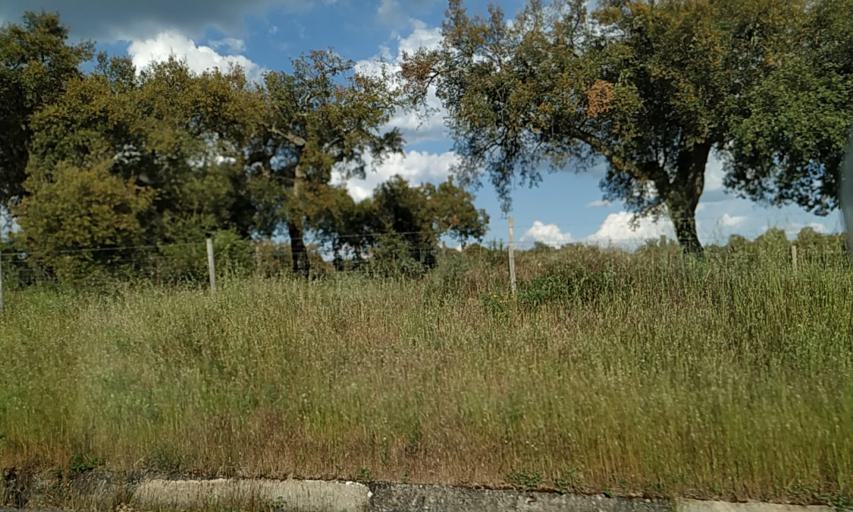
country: PT
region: Portalegre
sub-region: Portalegre
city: Urra
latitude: 39.2272
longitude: -7.4554
